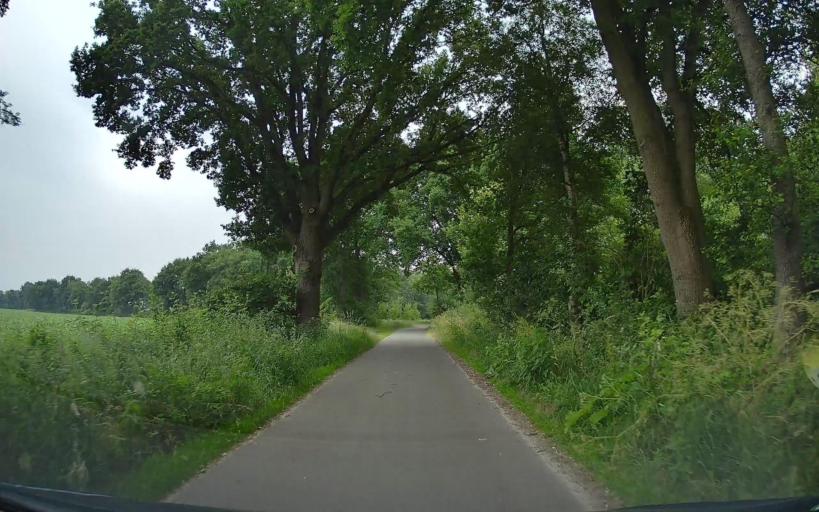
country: DE
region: Lower Saxony
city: Friesoythe
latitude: 53.0124
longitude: 7.8757
